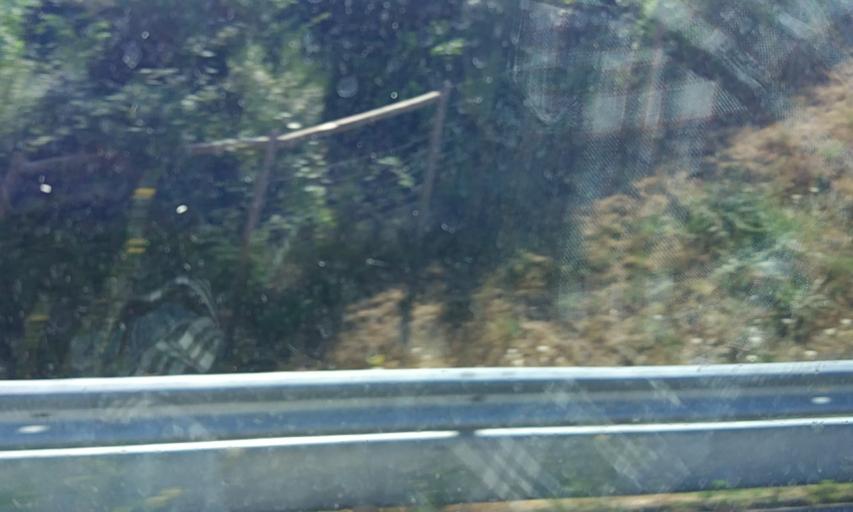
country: PT
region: Braganca
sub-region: Braganca Municipality
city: Braganca
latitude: 41.7473
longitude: -6.8094
